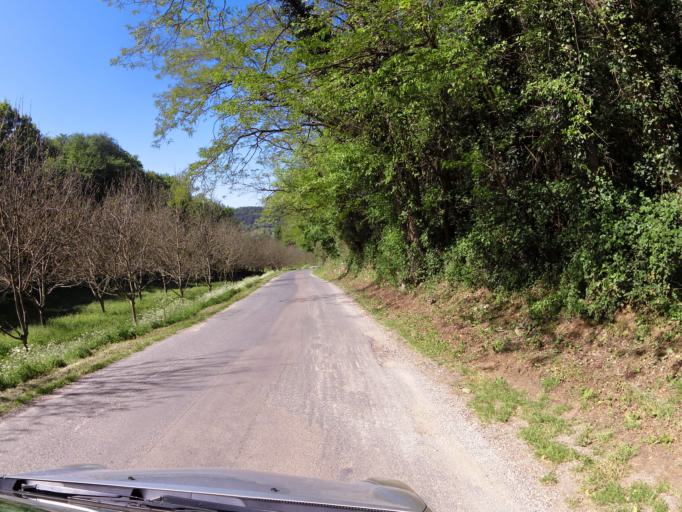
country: FR
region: Aquitaine
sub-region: Departement de la Dordogne
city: Saint-Cyprien
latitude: 44.8208
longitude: 1.1093
